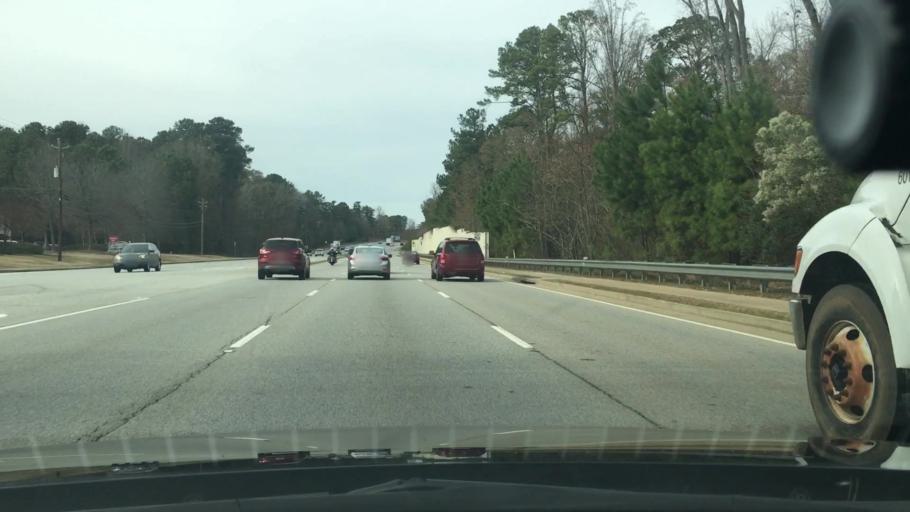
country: US
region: Georgia
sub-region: Fayette County
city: Peachtree City
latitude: 33.3769
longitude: -84.5734
